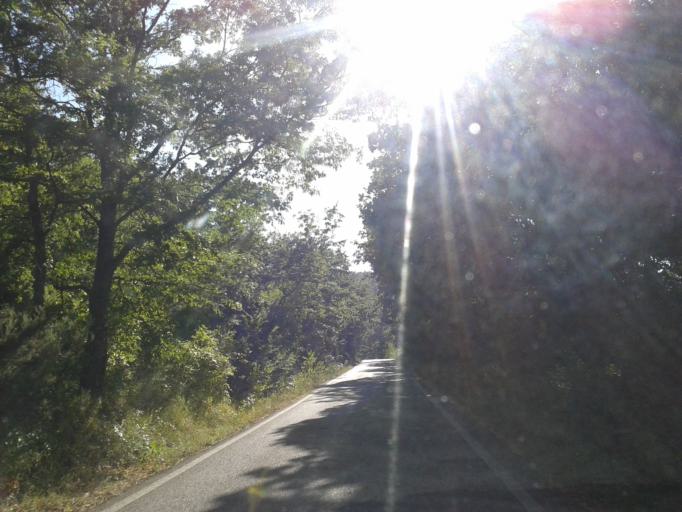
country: IT
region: Tuscany
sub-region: Province of Pisa
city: Chianni
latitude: 43.4536
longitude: 10.6296
